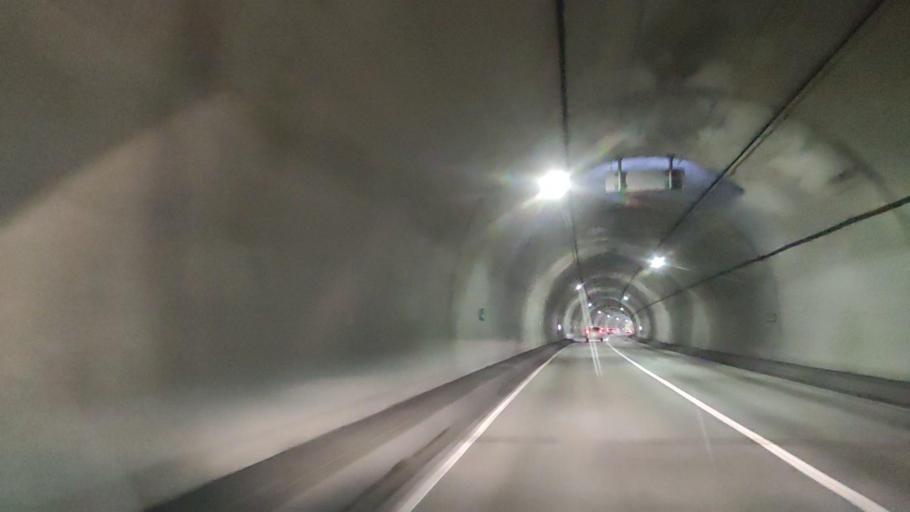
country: JP
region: Hokkaido
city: Ishikari
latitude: 43.5188
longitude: 141.3907
